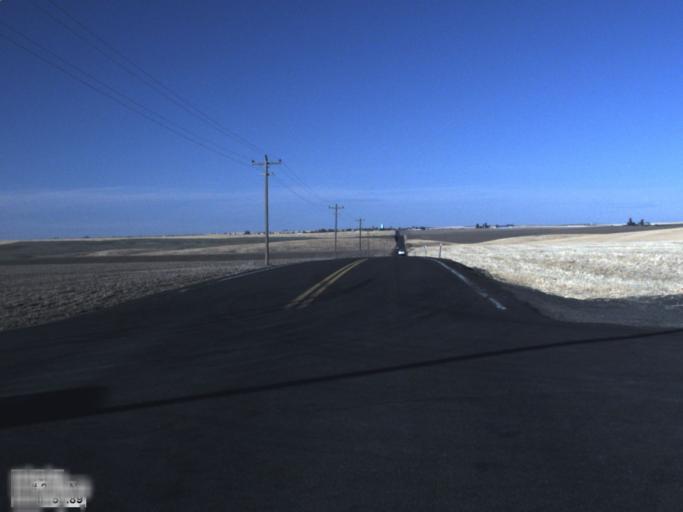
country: US
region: Washington
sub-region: Adams County
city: Ritzville
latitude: 47.0746
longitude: -118.3654
